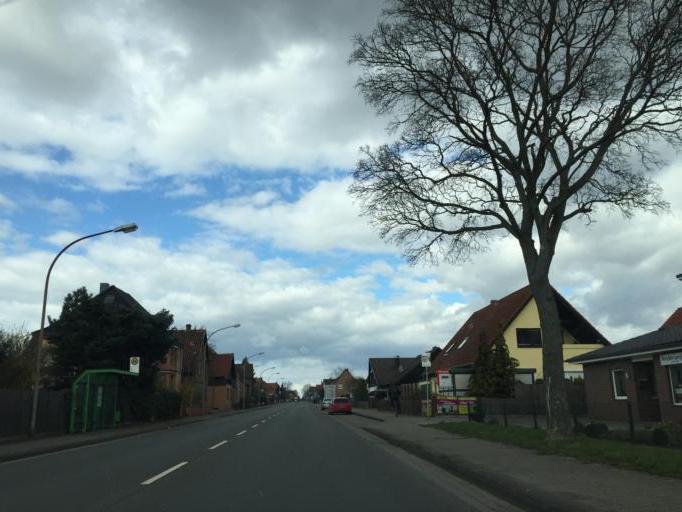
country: DE
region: Lower Saxony
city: Peine
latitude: 52.3404
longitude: 10.2393
